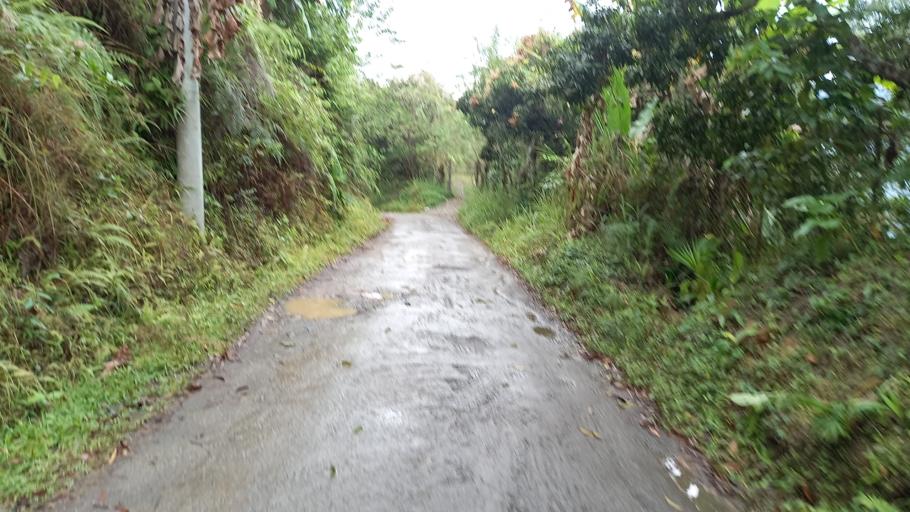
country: CO
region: Antioquia
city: Santa Barbara
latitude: 5.8446
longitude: -75.5750
